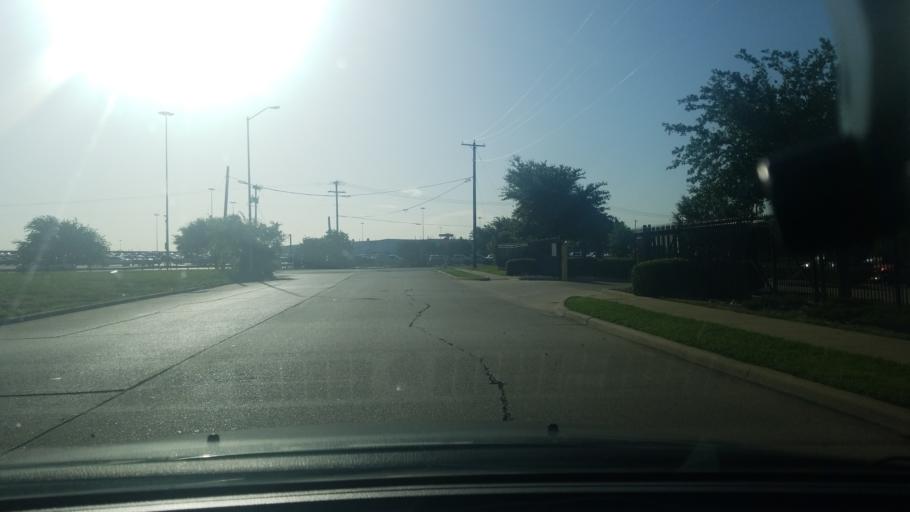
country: US
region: Texas
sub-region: Dallas County
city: Mesquite
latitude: 32.7840
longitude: -96.6692
